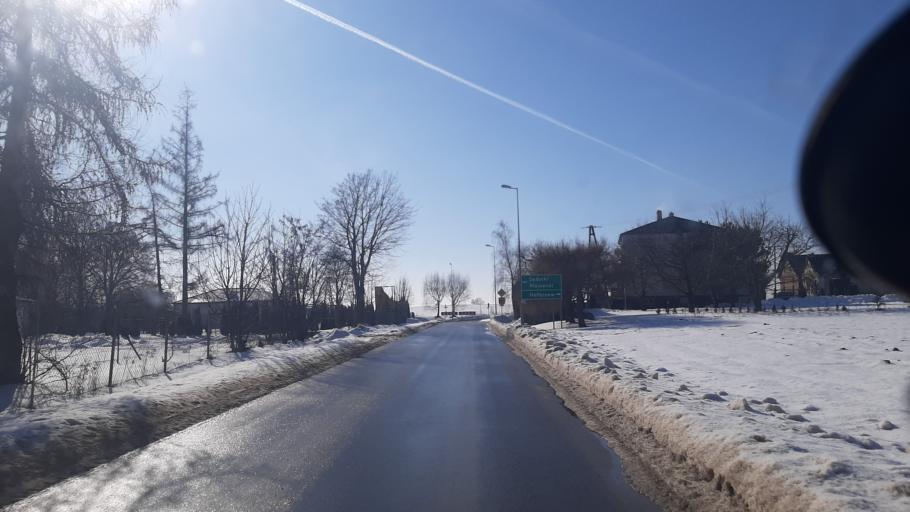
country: PL
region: Lublin Voivodeship
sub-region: Powiat lubelski
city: Garbow
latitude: 51.3065
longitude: 22.3059
